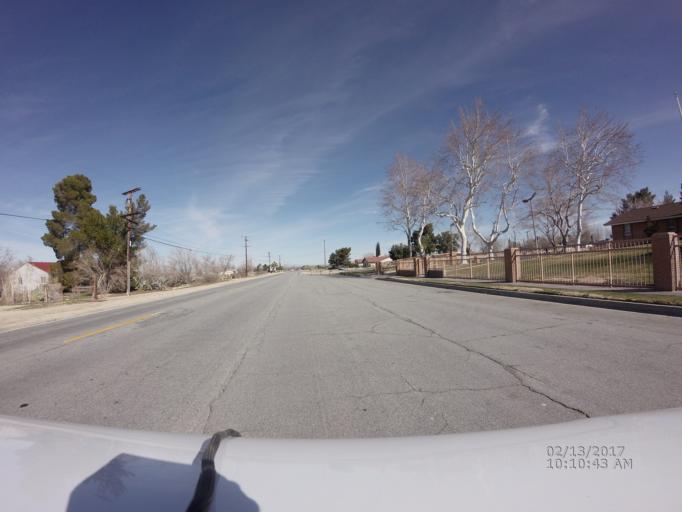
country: US
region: California
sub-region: Los Angeles County
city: Littlerock
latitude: 34.5228
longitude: -117.9747
